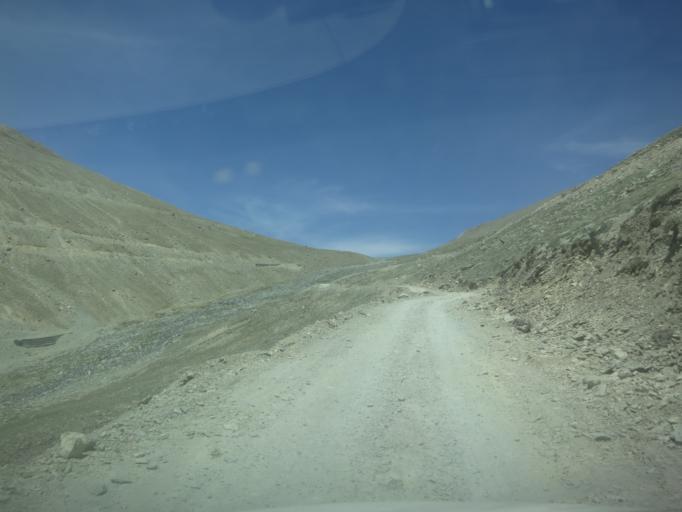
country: IN
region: Himachal Pradesh
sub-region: Kulu
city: Manali
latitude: 32.3861
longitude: 77.6226
